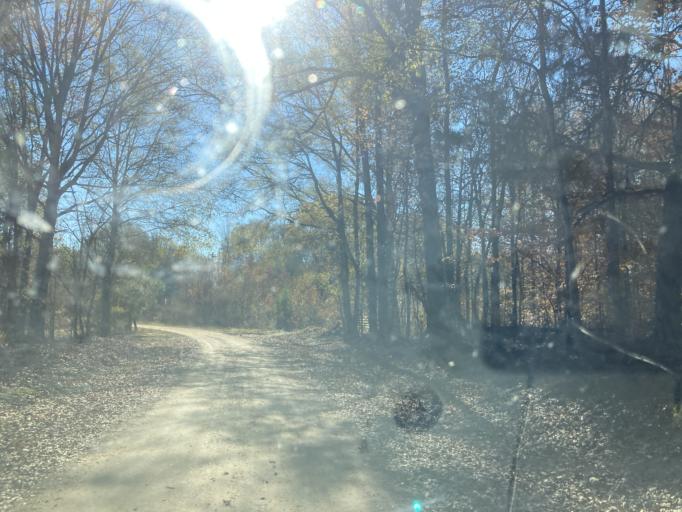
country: US
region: Mississippi
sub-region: Madison County
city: Kearney Park
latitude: 32.6177
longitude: -90.4563
